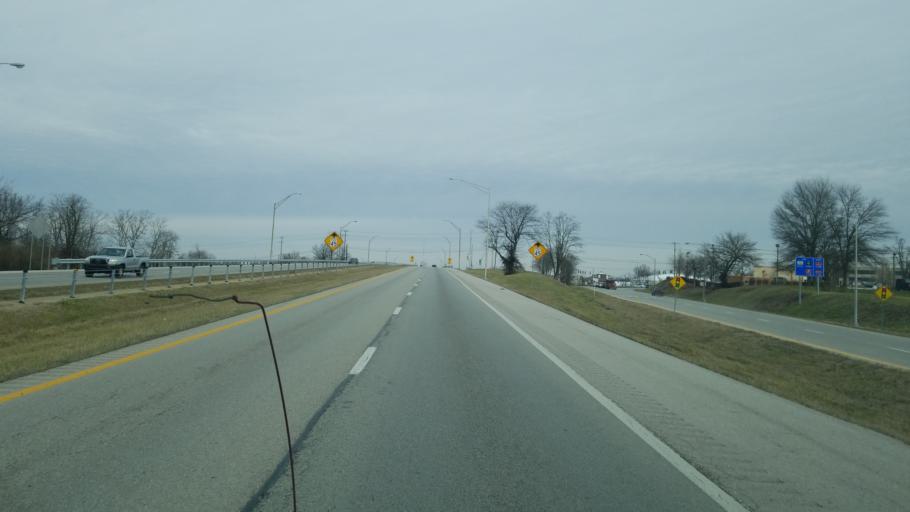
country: US
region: Kentucky
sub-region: Fayette County
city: Lexington
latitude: 38.0097
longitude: -84.4594
